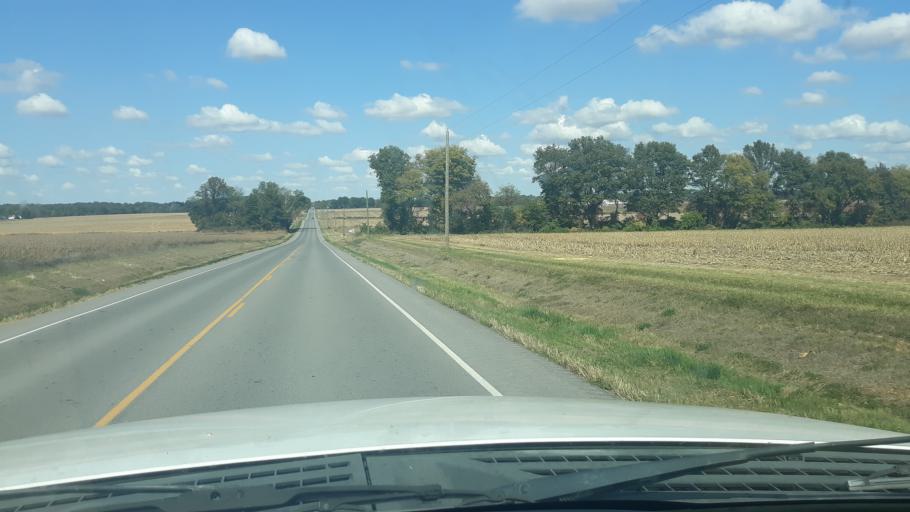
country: US
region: Illinois
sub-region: Saline County
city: Eldorado
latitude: 37.7957
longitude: -88.4848
